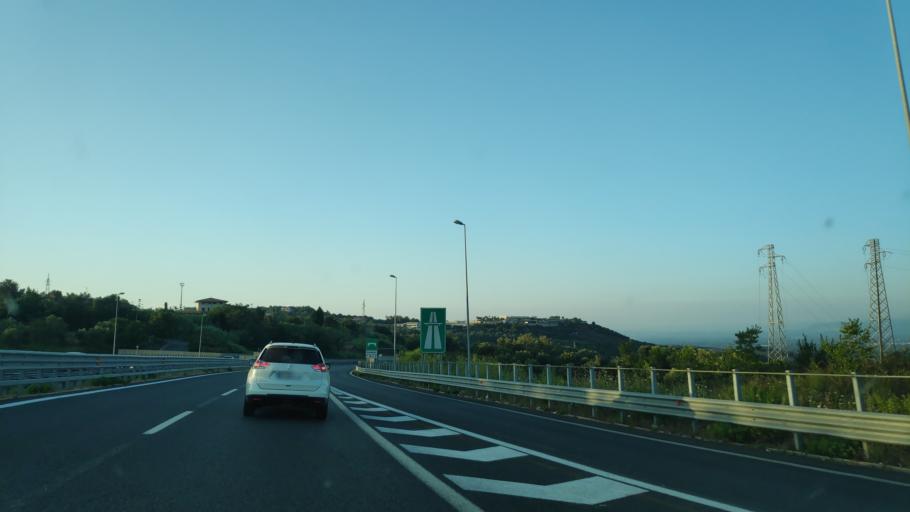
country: IT
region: Calabria
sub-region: Provincia di Reggio Calabria
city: Seminara
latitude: 38.3686
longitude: 15.8658
